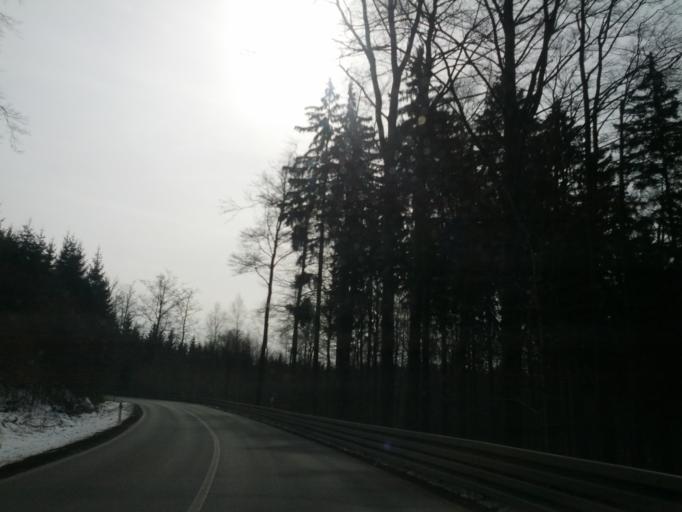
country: DE
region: Thuringia
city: Steinbach
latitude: 50.8540
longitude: 10.3764
